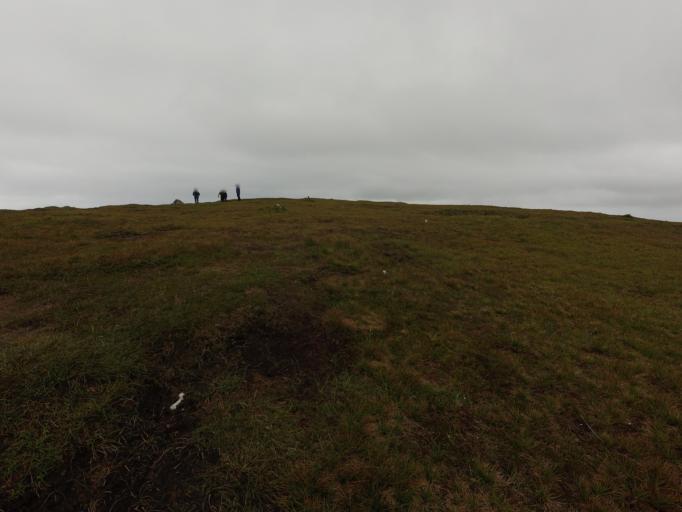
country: IE
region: Ulster
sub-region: County Donegal
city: Killybegs
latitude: 54.6484
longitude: -8.6930
